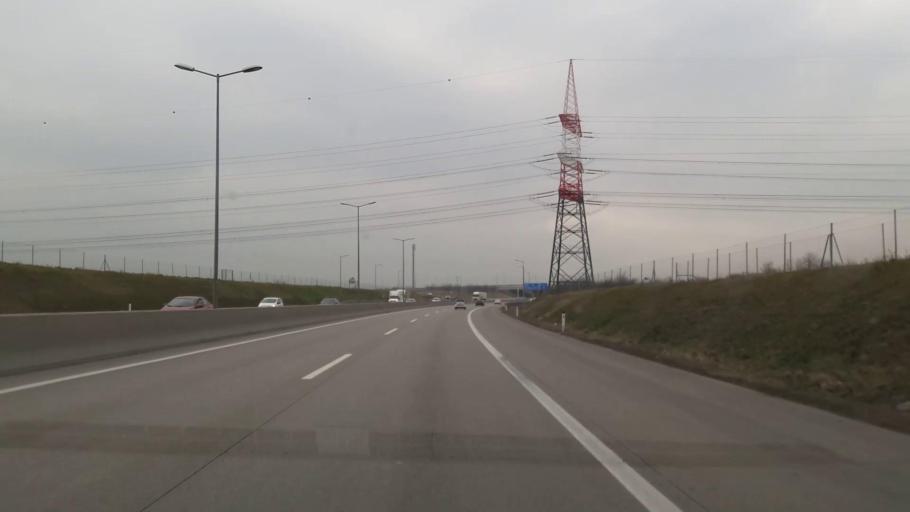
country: AT
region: Lower Austria
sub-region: Politischer Bezirk Wien-Umgebung
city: Leopoldsdorf
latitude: 48.1194
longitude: 16.4182
